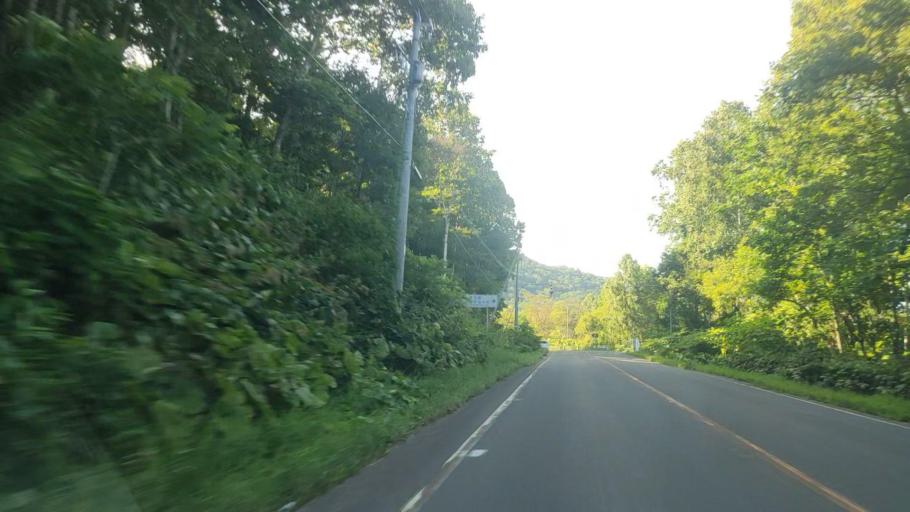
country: JP
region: Hokkaido
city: Nayoro
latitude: 44.7371
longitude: 142.1885
